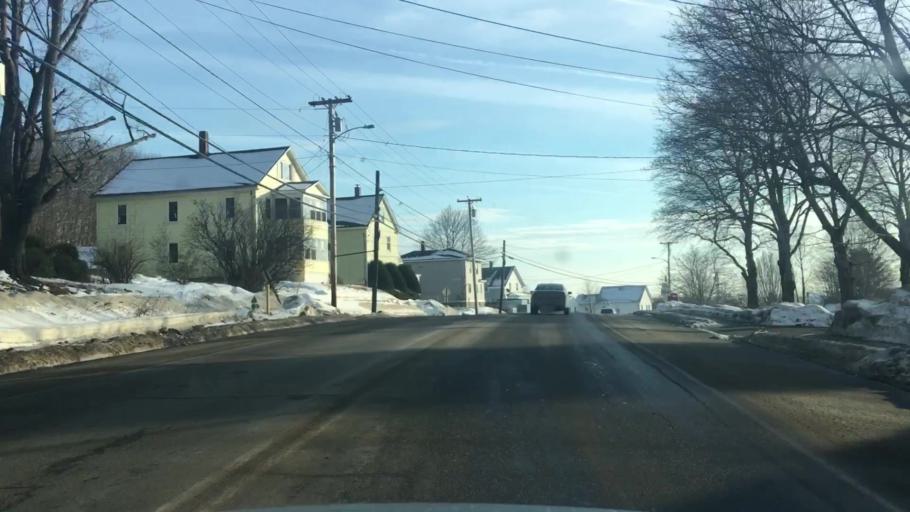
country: US
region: Maine
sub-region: Kennebec County
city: Augusta
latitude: 44.3312
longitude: -69.7765
